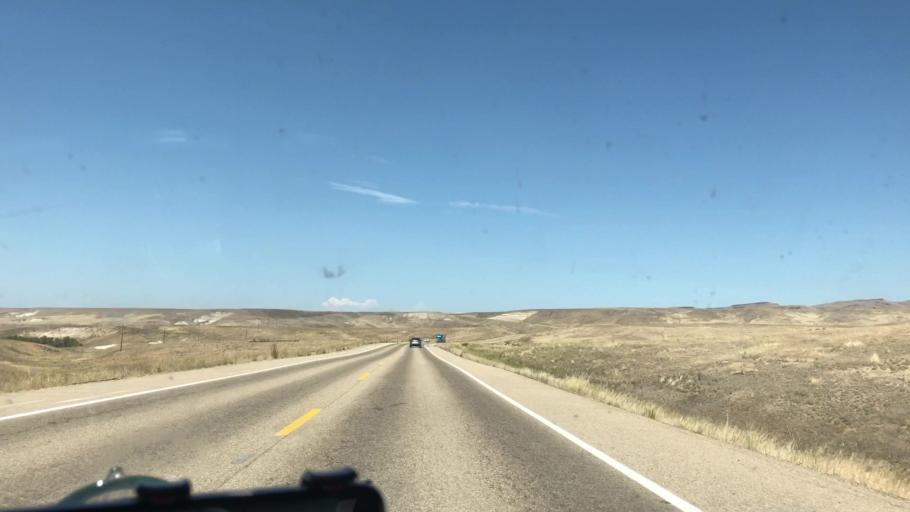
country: US
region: Idaho
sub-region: Owyhee County
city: Marsing
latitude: 43.2694
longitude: -117.0027
